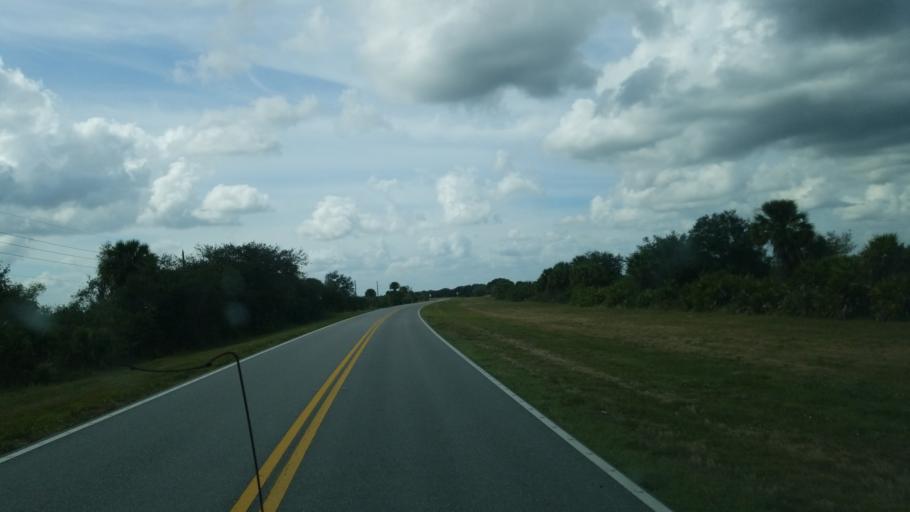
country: US
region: Florida
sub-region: Okeechobee County
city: Cypress Quarters
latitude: 27.4487
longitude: -80.6816
